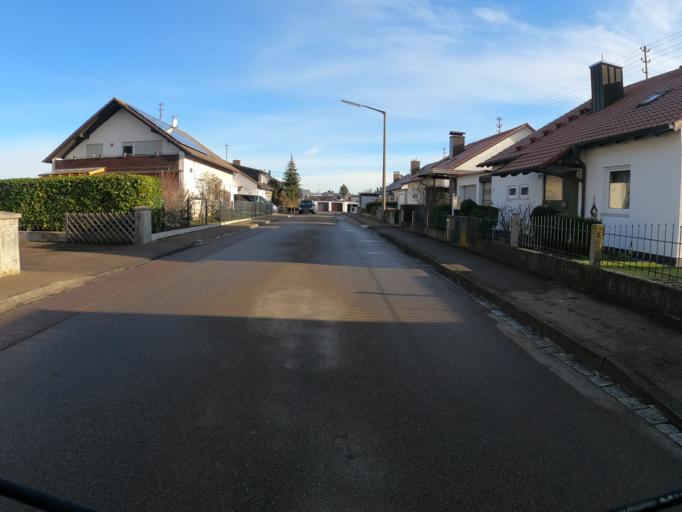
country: DE
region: Bavaria
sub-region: Swabia
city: Nersingen
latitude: 48.4199
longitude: 10.1559
